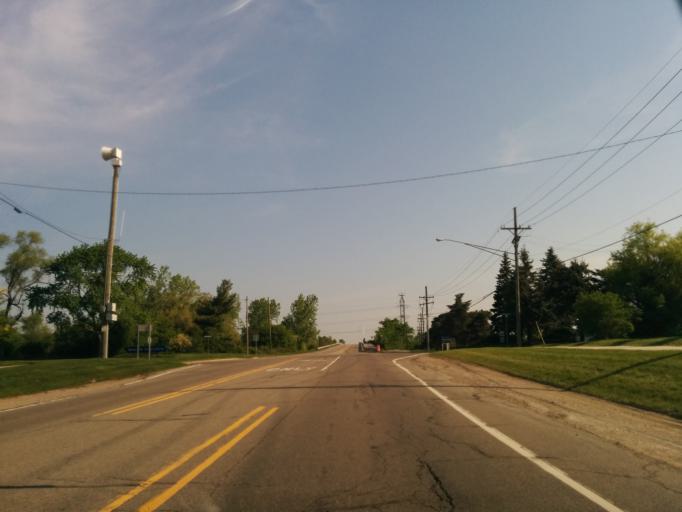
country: US
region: Michigan
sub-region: Oakland County
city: Novi
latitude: 42.4820
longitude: -83.4558
